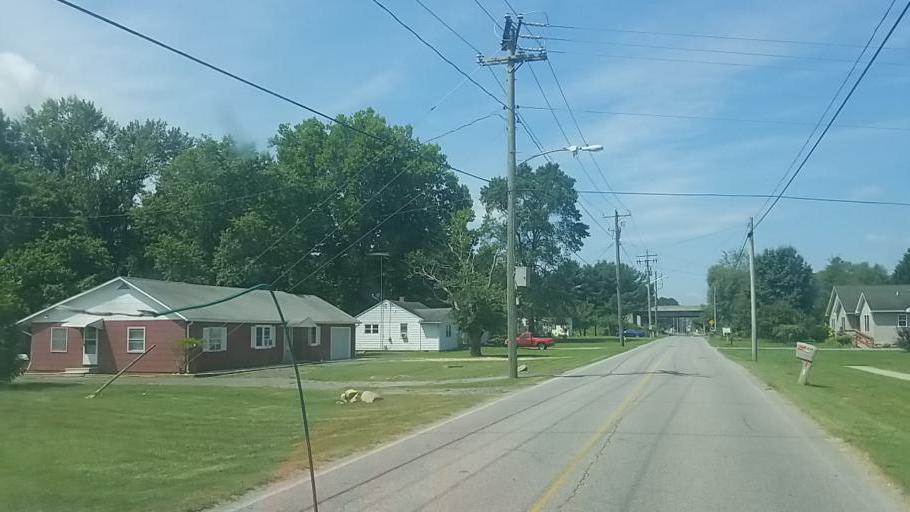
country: US
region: Maryland
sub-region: Caroline County
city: Denton
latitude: 38.8838
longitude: -75.8122
